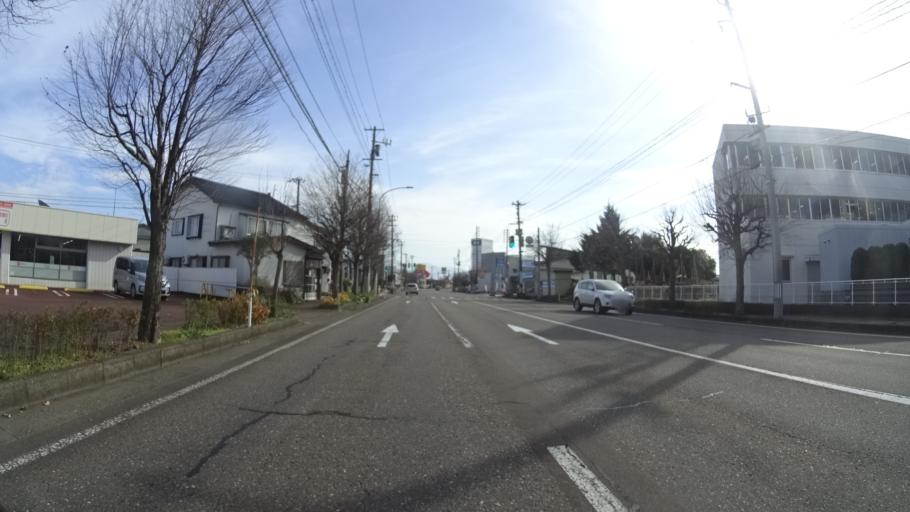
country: JP
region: Niigata
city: Joetsu
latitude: 37.1242
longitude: 138.2505
